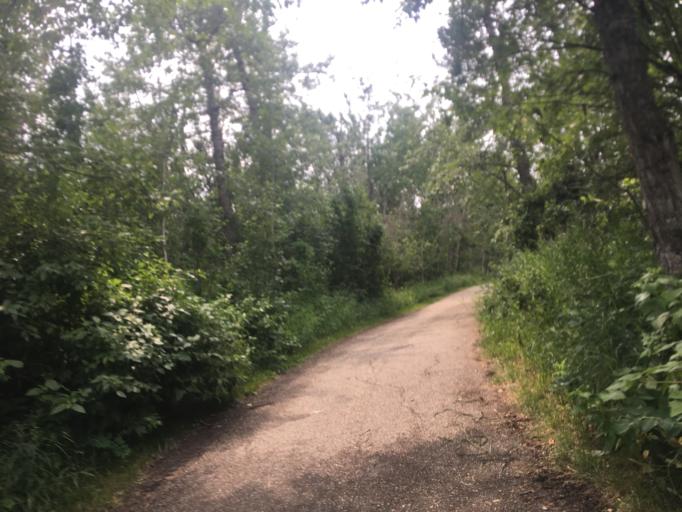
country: CA
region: Alberta
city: Grande Prairie
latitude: 55.1534
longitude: -118.8026
